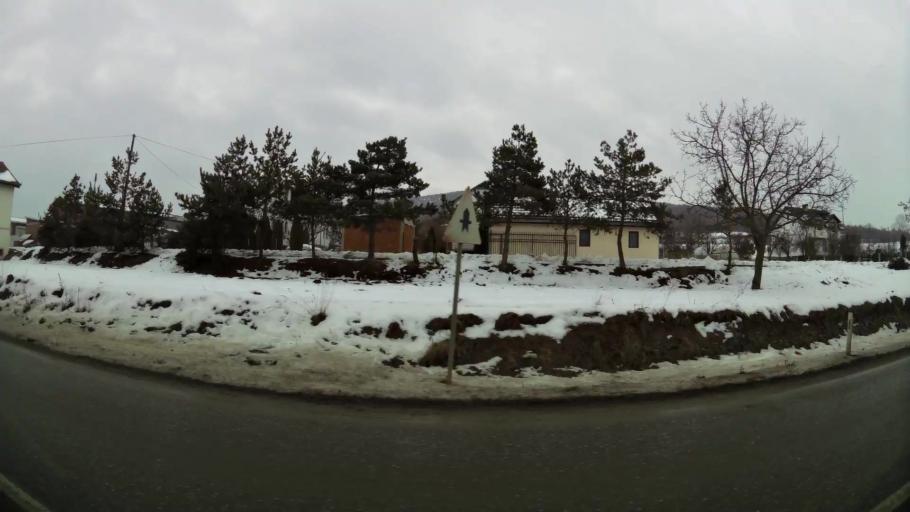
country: XK
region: Pristina
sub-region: Komuna e Prishtines
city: Pristina
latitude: 42.7278
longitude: 21.1440
